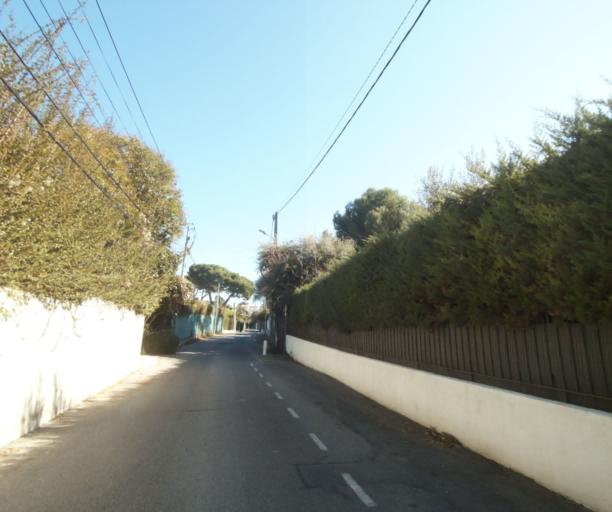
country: FR
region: Provence-Alpes-Cote d'Azur
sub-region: Departement des Alpes-Maritimes
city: Antibes
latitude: 43.5546
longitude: 7.1234
